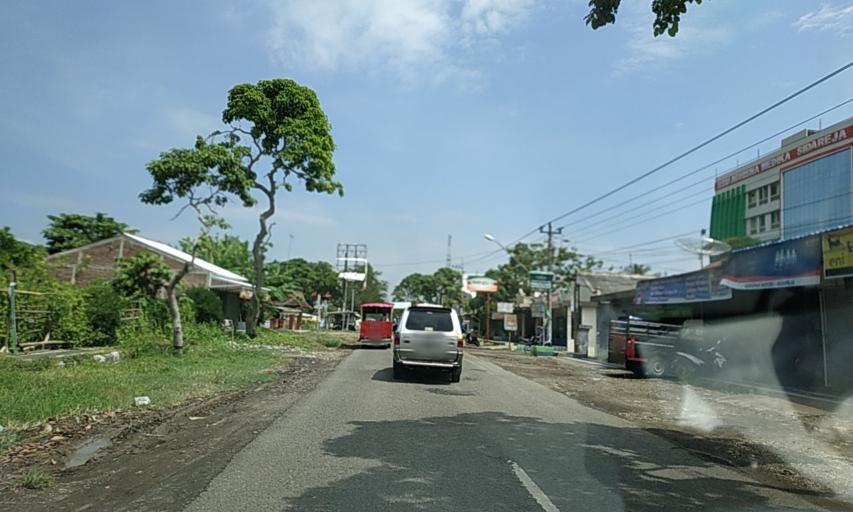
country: ID
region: Central Java
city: Sidamulya
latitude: -7.4857
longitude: 108.8006
